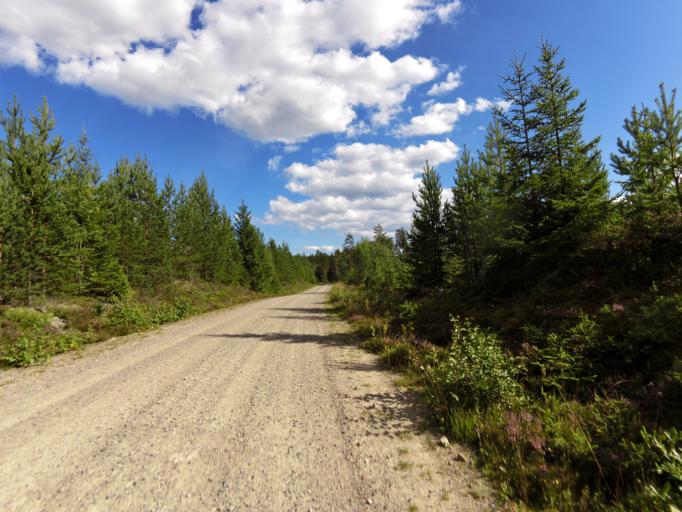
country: SE
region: Dalarna
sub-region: Faluns Kommun
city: Svardsjo
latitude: 60.6619
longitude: 15.9066
